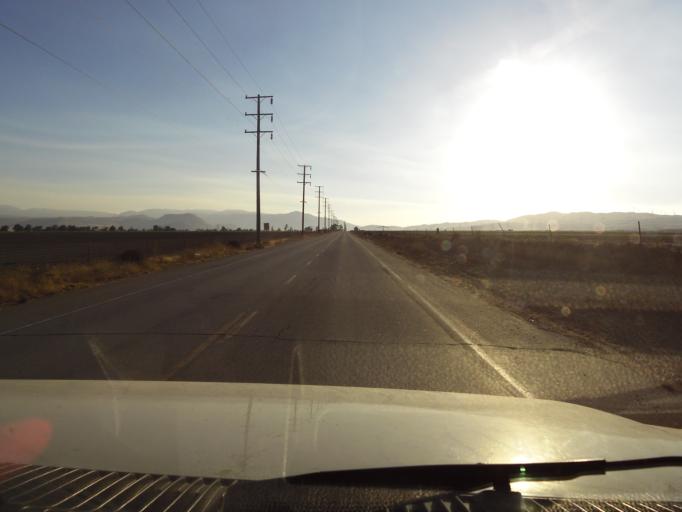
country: US
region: California
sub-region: Kern County
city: Tehachapi
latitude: 35.1096
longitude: -118.4224
